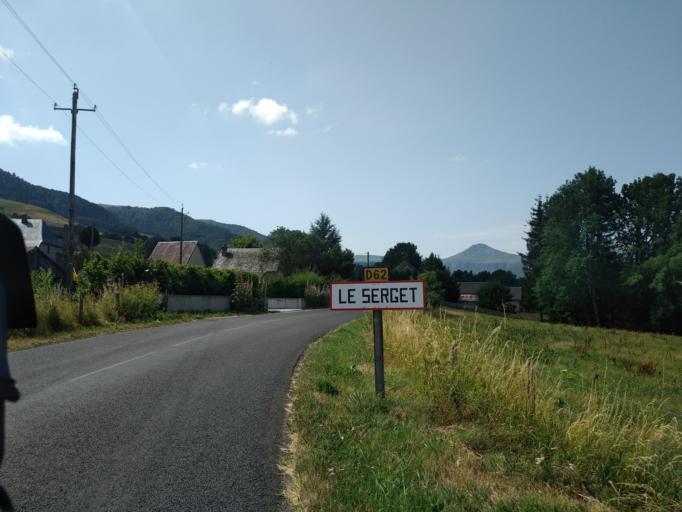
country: FR
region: Auvergne
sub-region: Departement du Cantal
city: Riom-es-Montagnes
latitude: 45.1684
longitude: 2.7142
